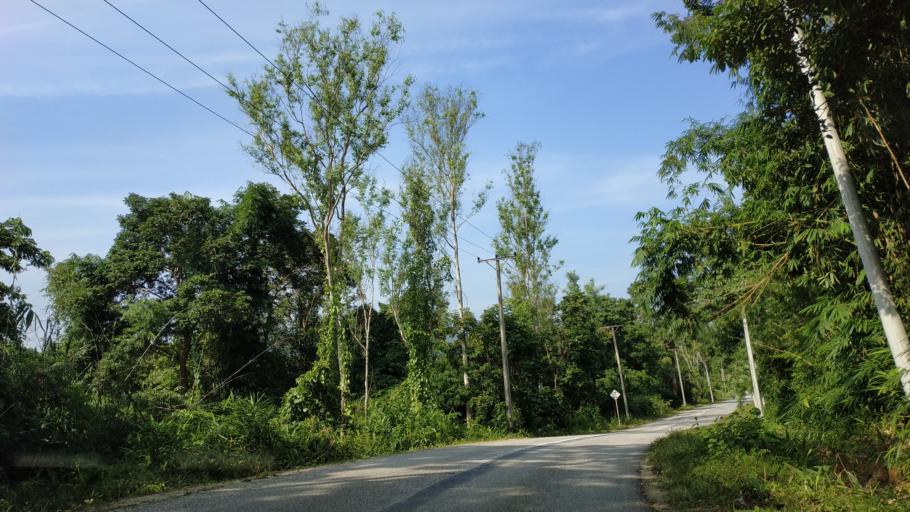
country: MM
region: Tanintharyi
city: Dawei
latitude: 14.5998
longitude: 98.0959
